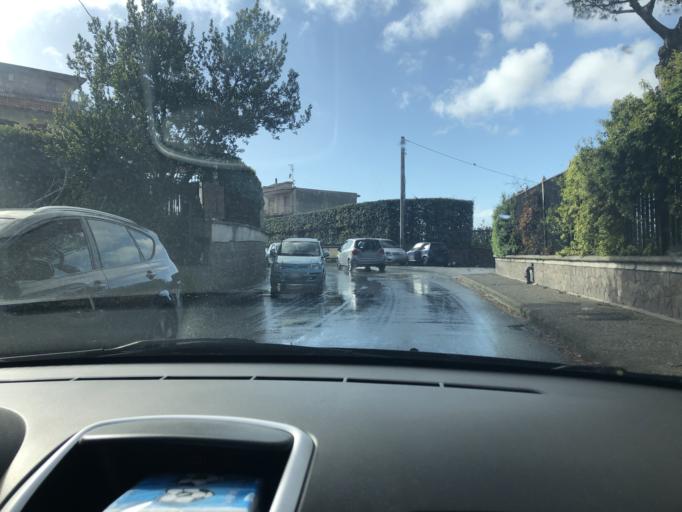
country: IT
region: Campania
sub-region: Provincia di Napoli
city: Torre Caracciolo
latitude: 40.8754
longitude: 14.1814
